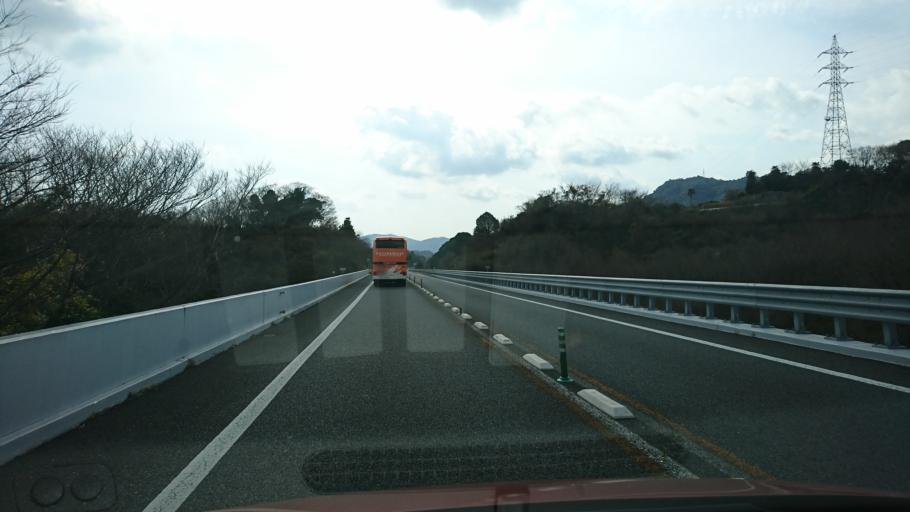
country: JP
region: Hiroshima
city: Innoshima
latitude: 34.2391
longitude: 133.0480
